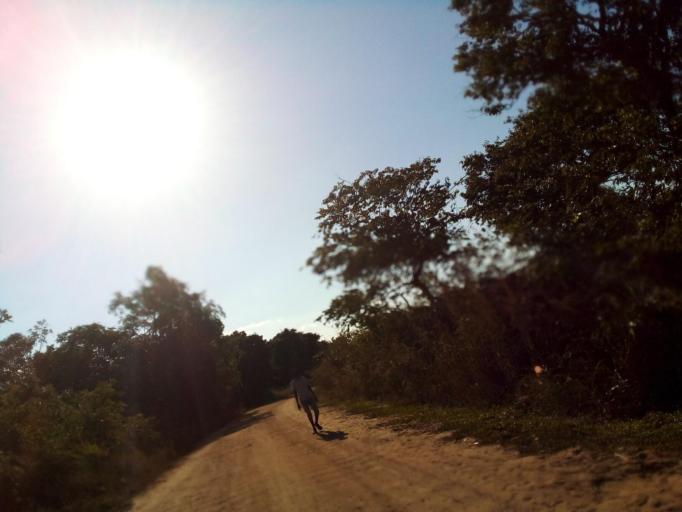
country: MZ
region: Zambezia
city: Quelimane
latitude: -17.4819
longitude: 36.5442
